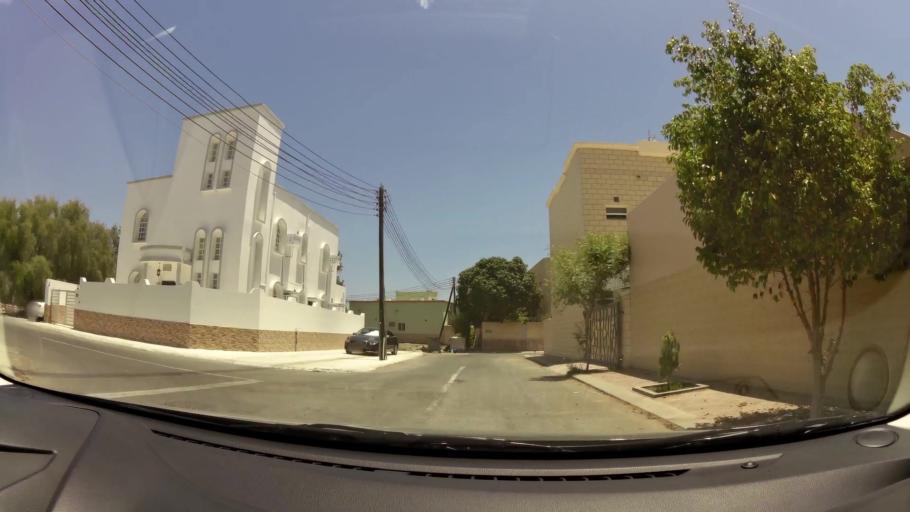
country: OM
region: Muhafazat Masqat
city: As Sib al Jadidah
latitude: 23.6322
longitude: 58.2434
